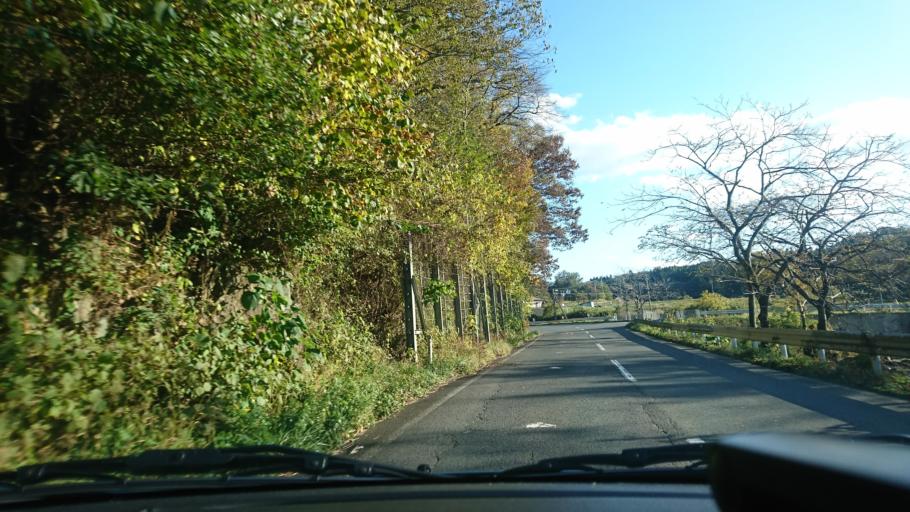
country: JP
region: Iwate
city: Ichinoseki
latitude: 38.8575
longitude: 141.3326
